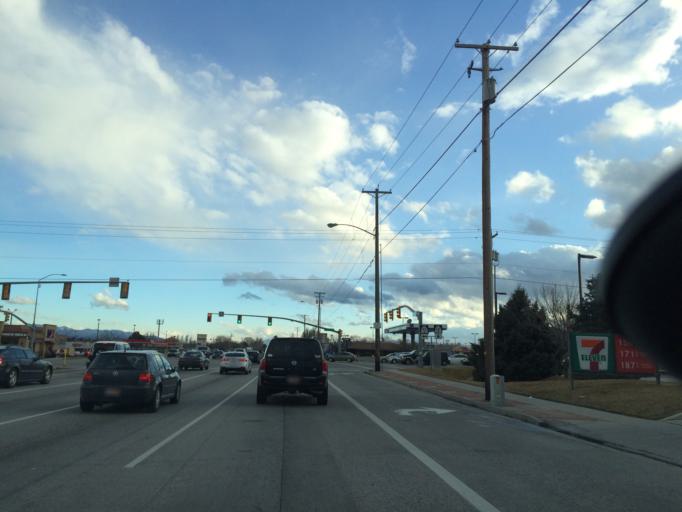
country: US
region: Utah
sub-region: Salt Lake County
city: West Jordan
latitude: 40.6249
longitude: -111.9390
